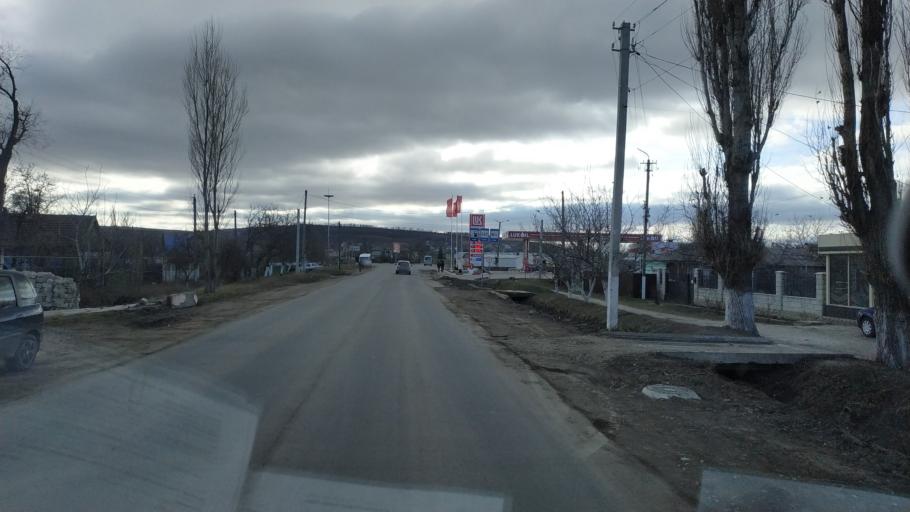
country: MD
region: Causeni
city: Causeni
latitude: 46.6511
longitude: 29.4084
